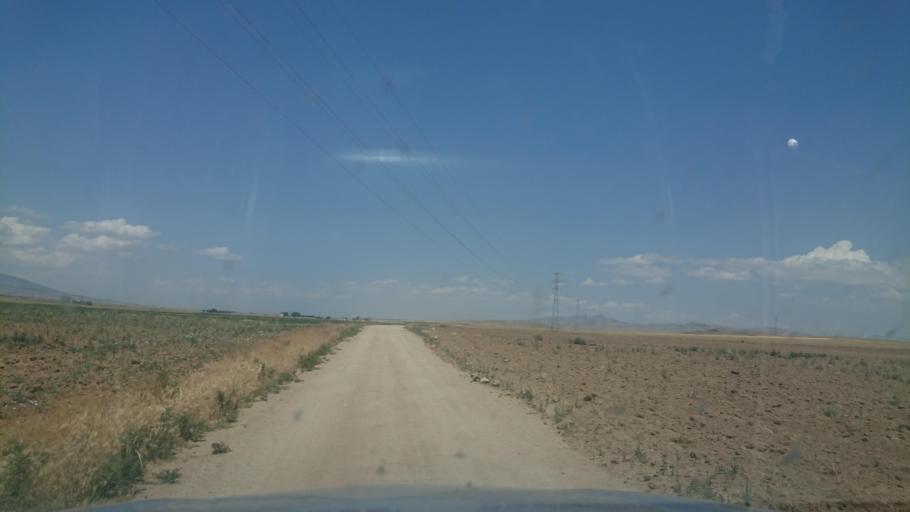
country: TR
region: Aksaray
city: Sariyahsi
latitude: 39.0106
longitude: 33.8806
